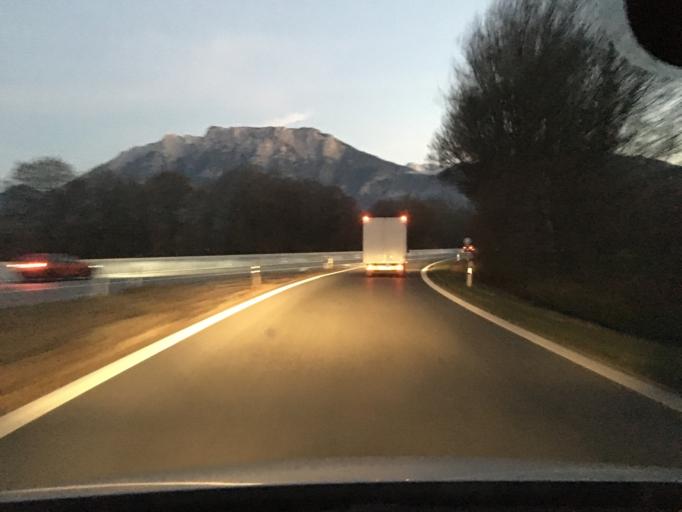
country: DE
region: Bavaria
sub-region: Upper Bavaria
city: Oberaudorf
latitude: 47.6452
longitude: 12.1898
